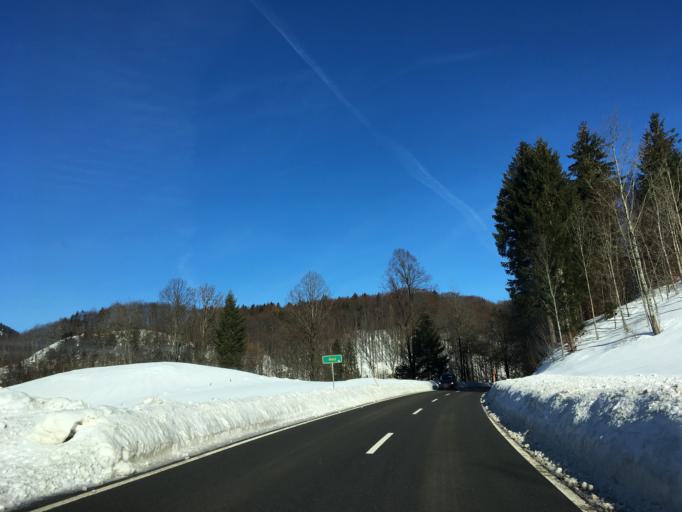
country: DE
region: Bavaria
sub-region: Upper Bavaria
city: Aschau im Chiemgau
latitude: 47.7541
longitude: 12.3159
